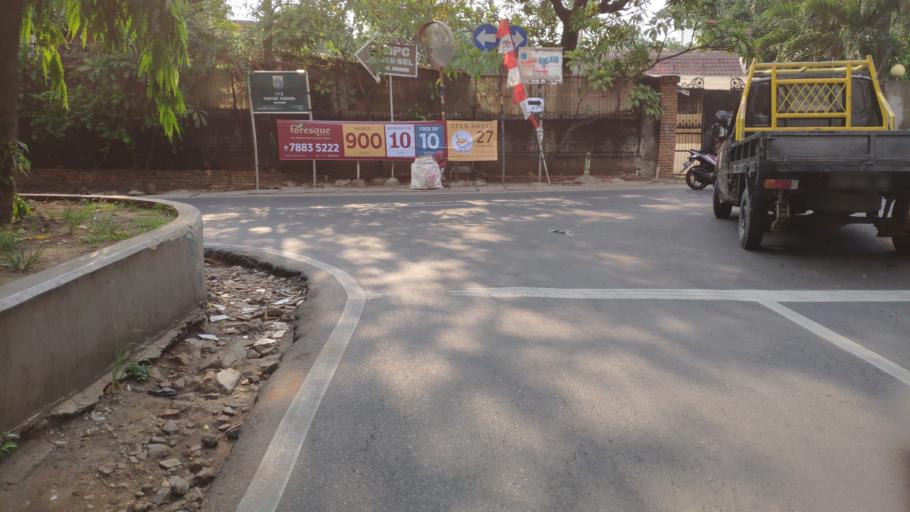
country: ID
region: West Java
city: Pamulang
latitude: -6.3158
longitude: 106.8118
